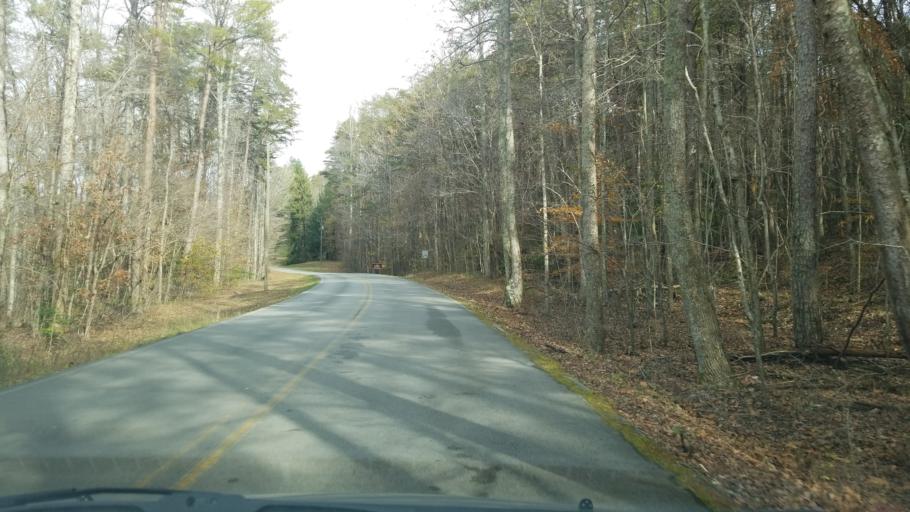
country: US
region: Georgia
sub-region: Dade County
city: Trenton
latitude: 34.8251
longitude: -85.4829
